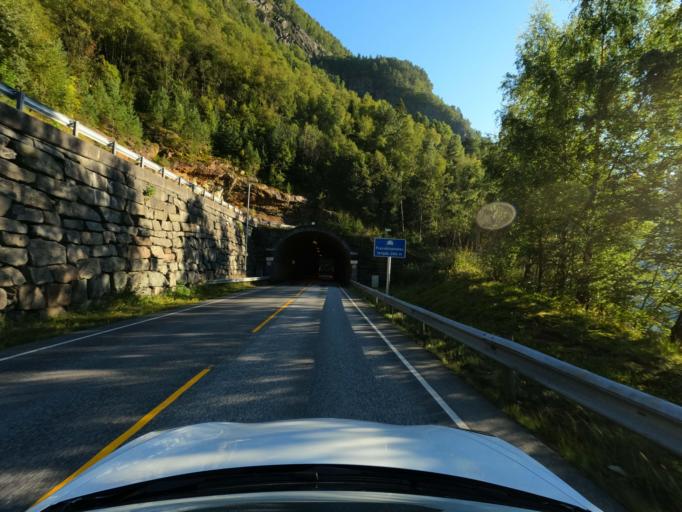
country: NO
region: Hordaland
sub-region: Odda
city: Odda
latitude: 60.1828
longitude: 6.5883
